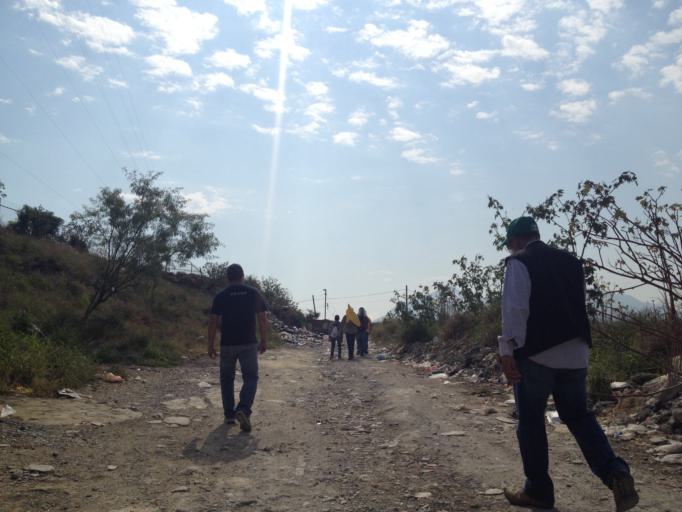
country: MX
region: Nuevo Leon
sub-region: Monterrey
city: Monterrey
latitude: 25.6532
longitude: -100.3283
